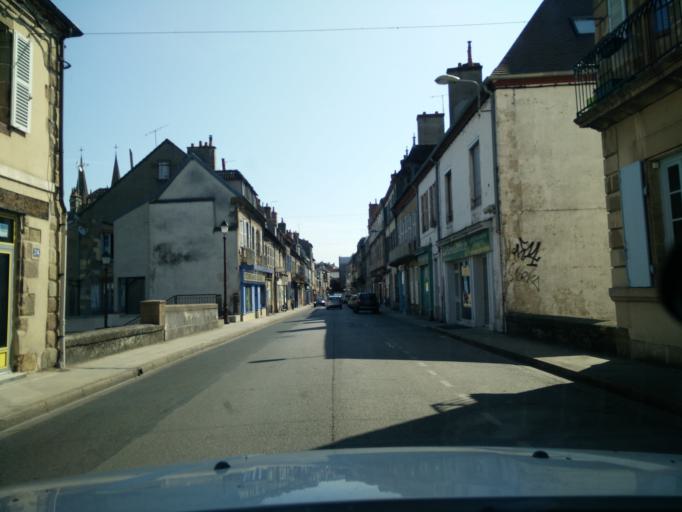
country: FR
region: Auvergne
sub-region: Departement de l'Allier
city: Moulins
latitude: 46.5629
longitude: 3.3262
